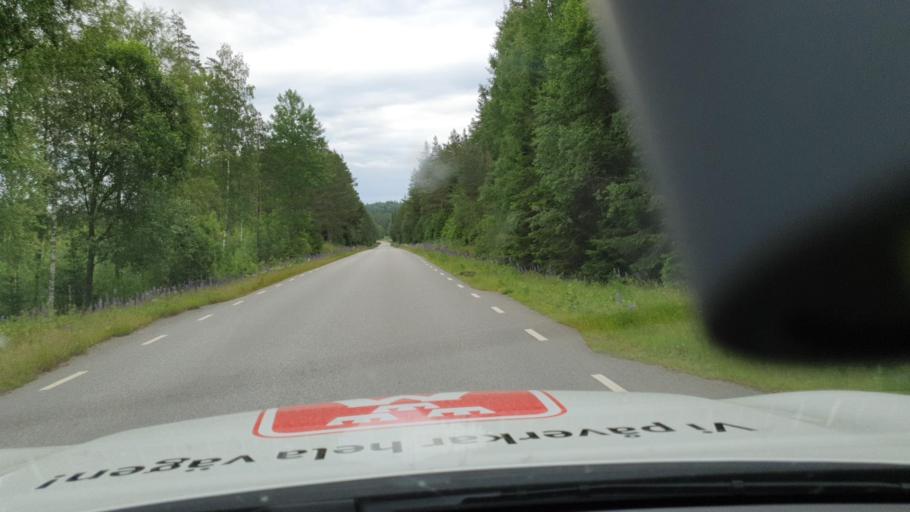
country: SE
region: Vaestra Goetaland
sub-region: Karlsborgs Kommun
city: Karlsborg
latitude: 58.6693
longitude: 14.4590
